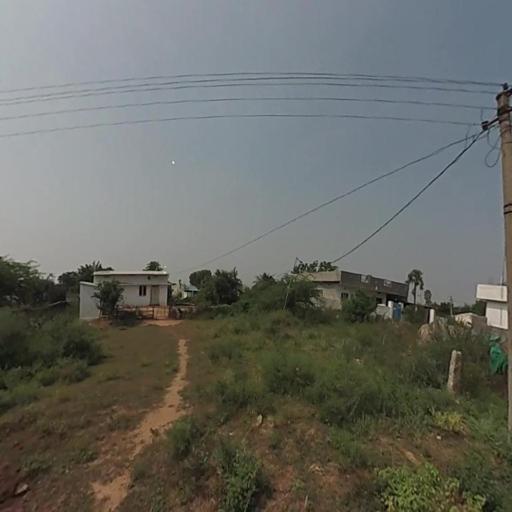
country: IN
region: Telangana
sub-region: Nalgonda
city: Nalgonda
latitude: 17.1936
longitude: 79.1334
